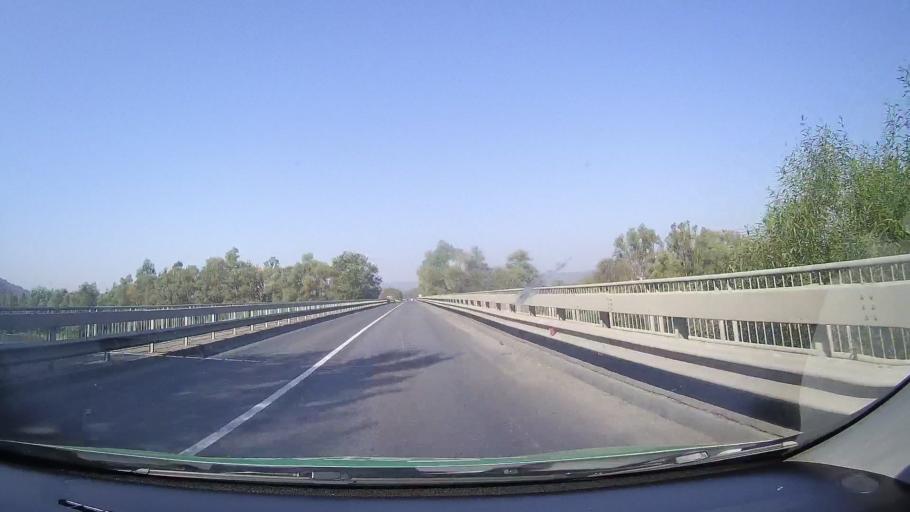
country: RO
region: Hunedoara
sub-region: Comuna Ilia
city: Ilia
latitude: 45.9241
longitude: 22.6689
